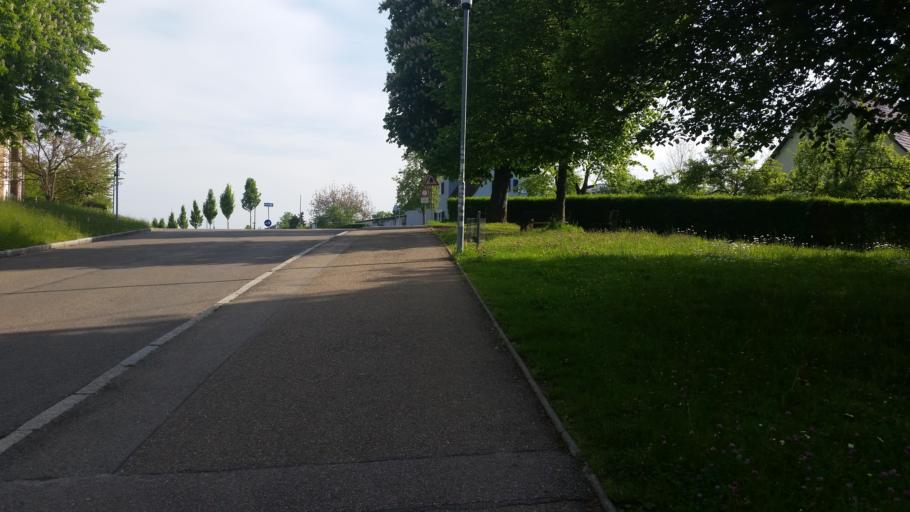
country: DE
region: Bavaria
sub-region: Swabia
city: Wertingen
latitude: 48.5642
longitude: 10.6809
